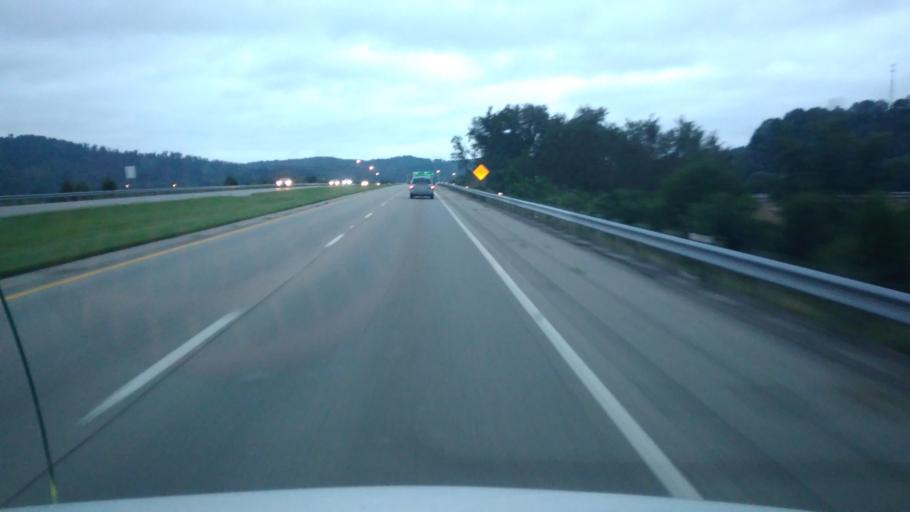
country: US
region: Ohio
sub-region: Ross County
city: Chillicothe
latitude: 39.2956
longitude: -82.9444
